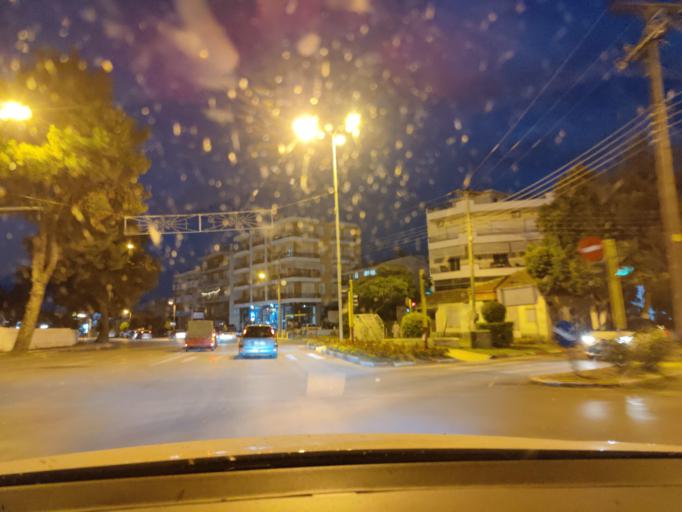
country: GR
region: Central Macedonia
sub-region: Nomos Serron
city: Serres
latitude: 41.0864
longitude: 23.5293
